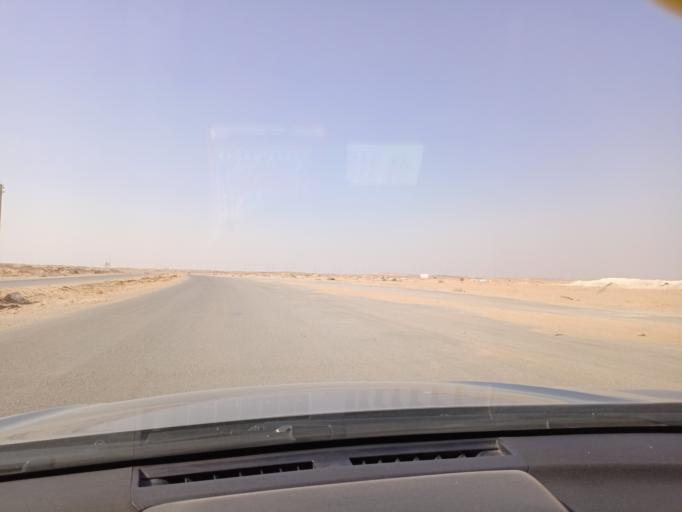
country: EG
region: Muhafazat al Qalyubiyah
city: Al Khankah
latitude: 30.0397
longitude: 31.7158
